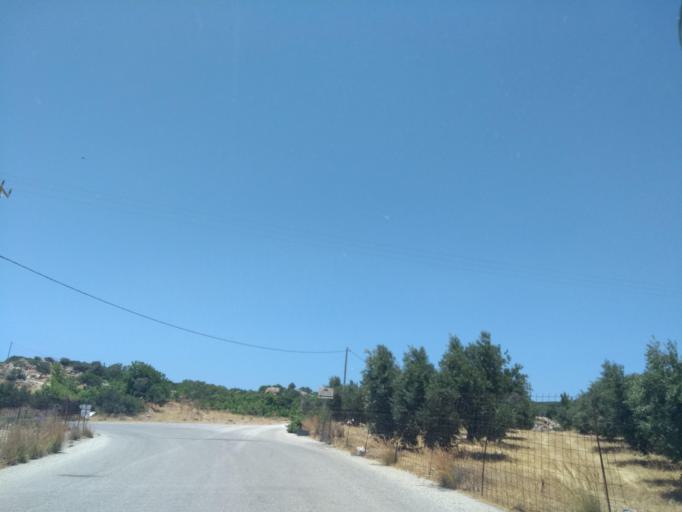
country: GR
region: Crete
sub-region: Nomos Chanias
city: Vryses
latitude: 35.3397
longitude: 23.5447
